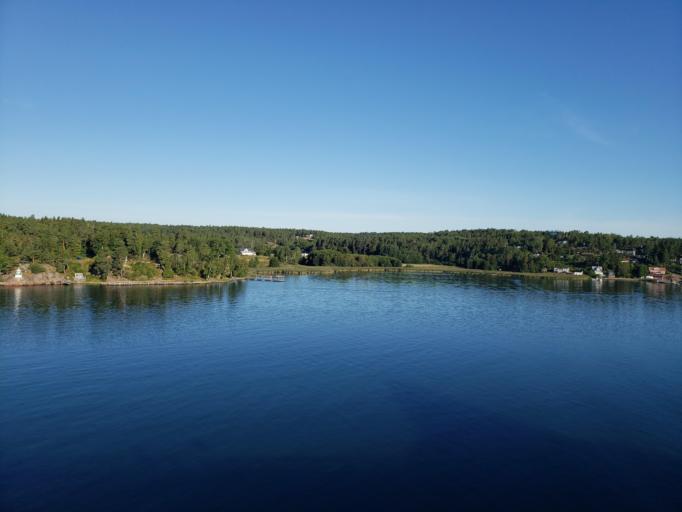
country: SE
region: Stockholm
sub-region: Vaxholms Kommun
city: Vaxholm
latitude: 59.4977
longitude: 18.4654
